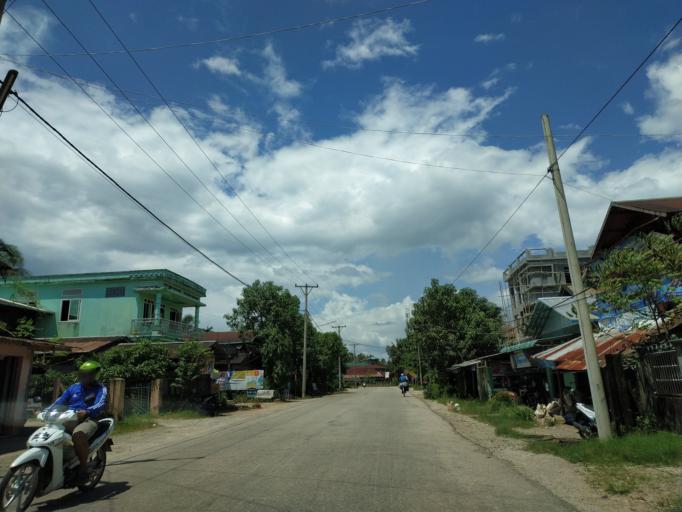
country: MM
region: Tanintharyi
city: Dawei
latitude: 14.1015
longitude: 98.1722
